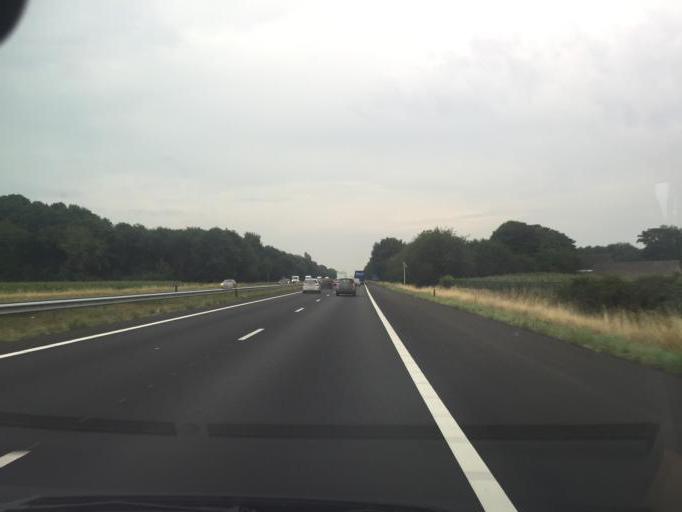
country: NL
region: North Brabant
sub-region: Gemeente Asten
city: Asten
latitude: 51.3989
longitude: 5.8334
